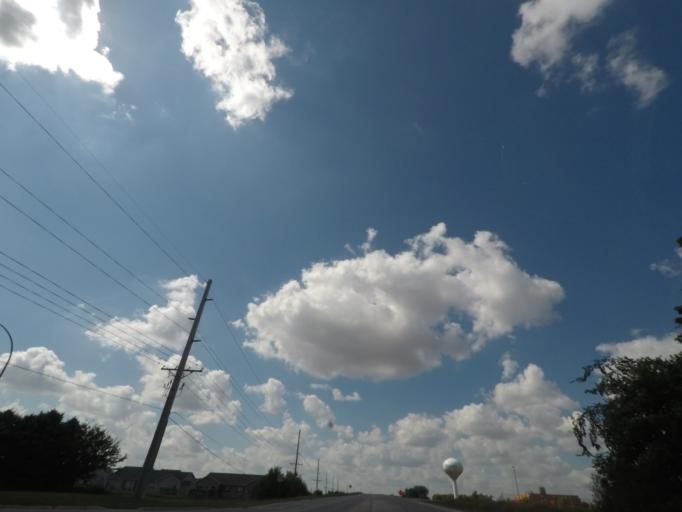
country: US
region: Iowa
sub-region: Story County
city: Nevada
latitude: 42.0229
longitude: -93.4722
